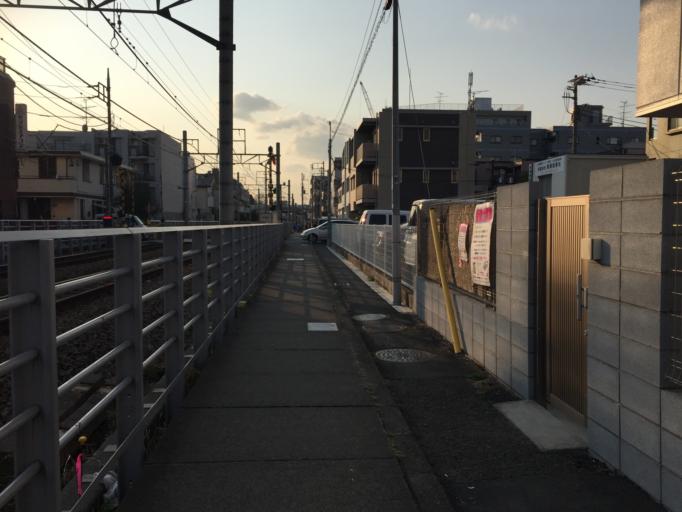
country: JP
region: Tokyo
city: Tokyo
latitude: 35.6076
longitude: 139.6518
